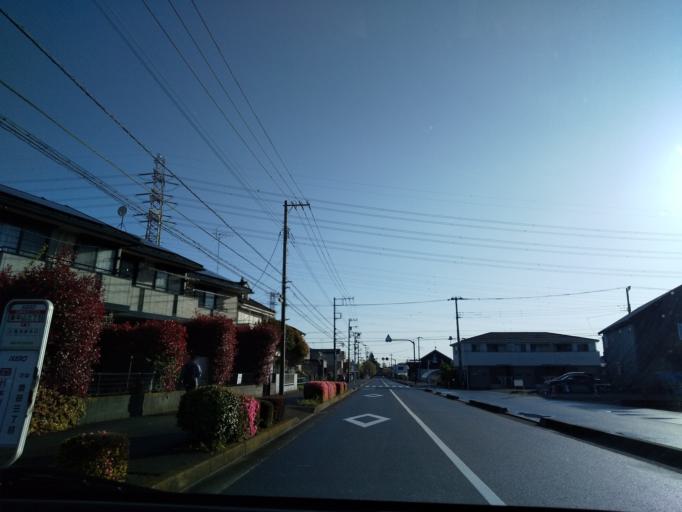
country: JP
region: Tokyo
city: Hino
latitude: 35.6525
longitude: 139.3762
